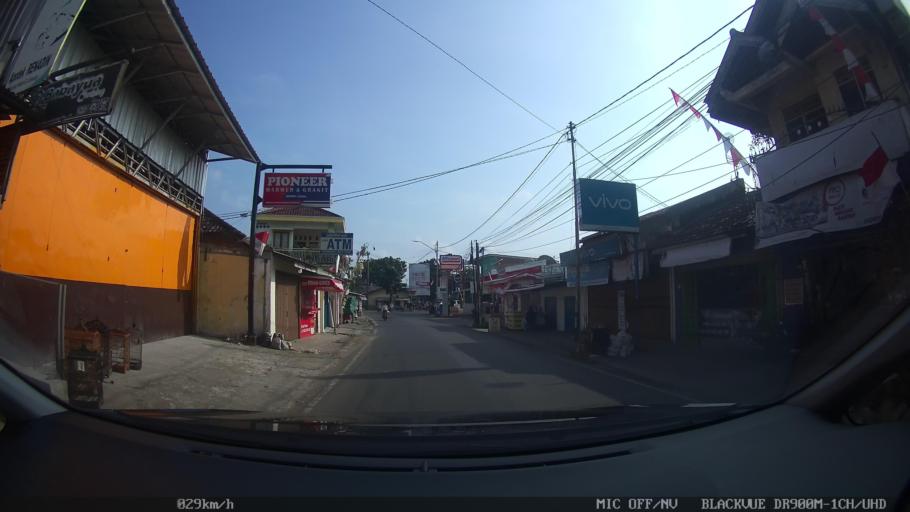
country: ID
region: Lampung
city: Kedaton
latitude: -5.3973
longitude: 105.2488
